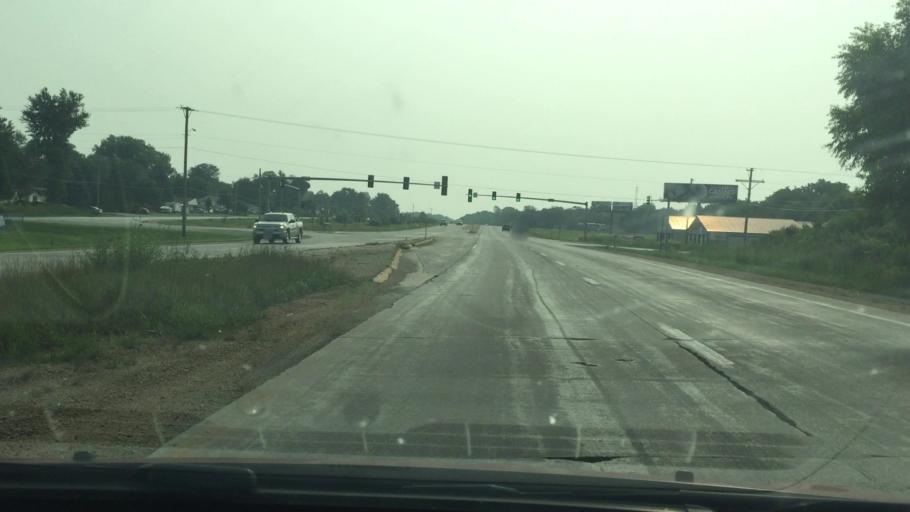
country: US
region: Iowa
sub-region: Scott County
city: Buffalo
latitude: 41.5084
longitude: -90.6897
